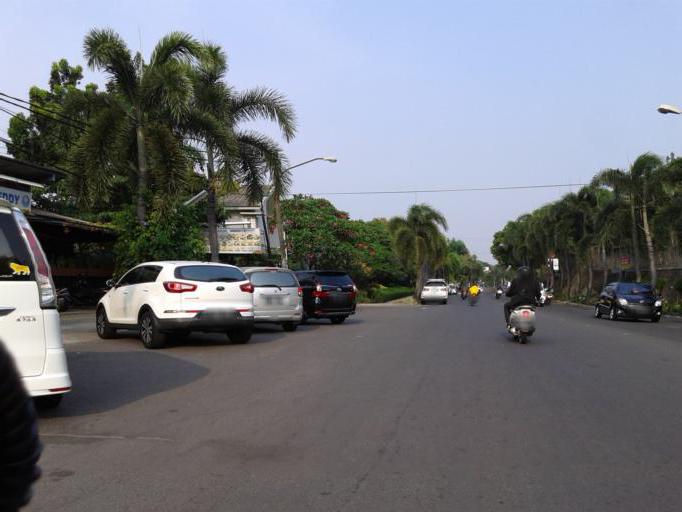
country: ID
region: Banten
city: South Tangerang
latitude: -6.2811
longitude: 106.7085
